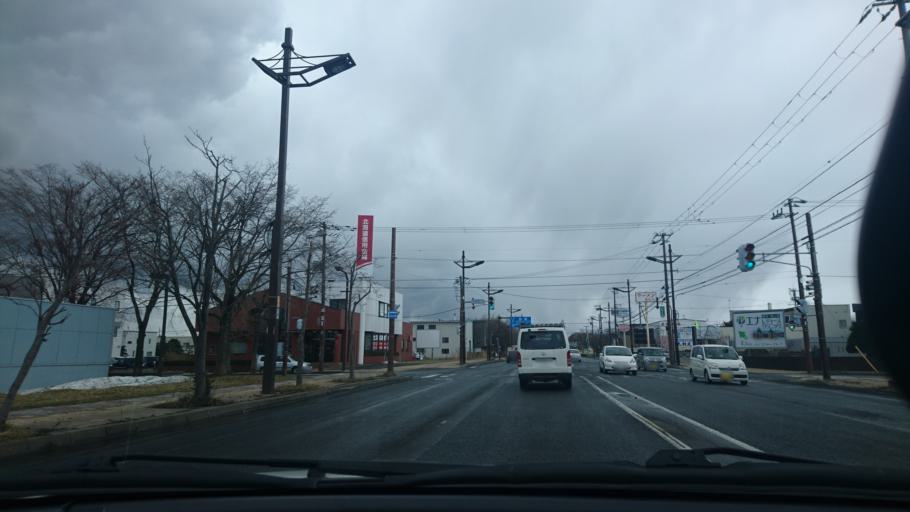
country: JP
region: Hokkaido
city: Ishikari
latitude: 43.1716
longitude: 141.3143
